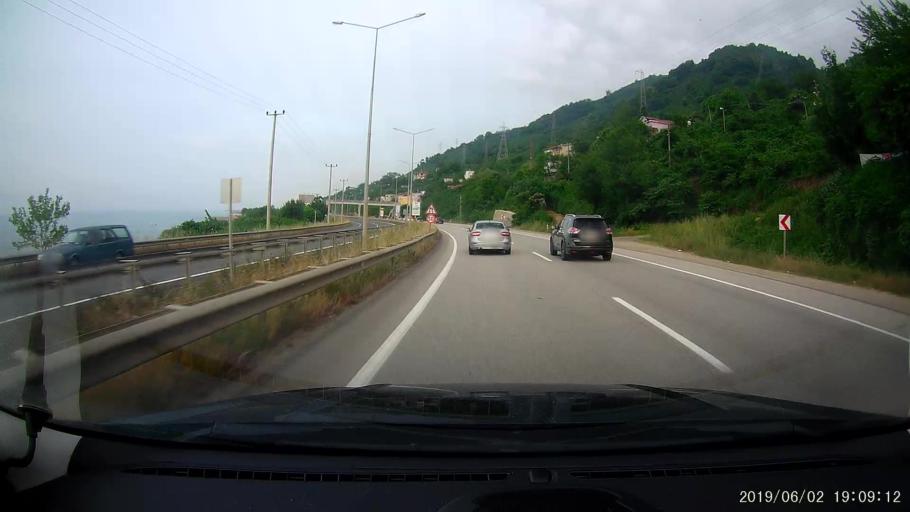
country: TR
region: Ordu
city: Gulyali
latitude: 40.9739
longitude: 38.0236
